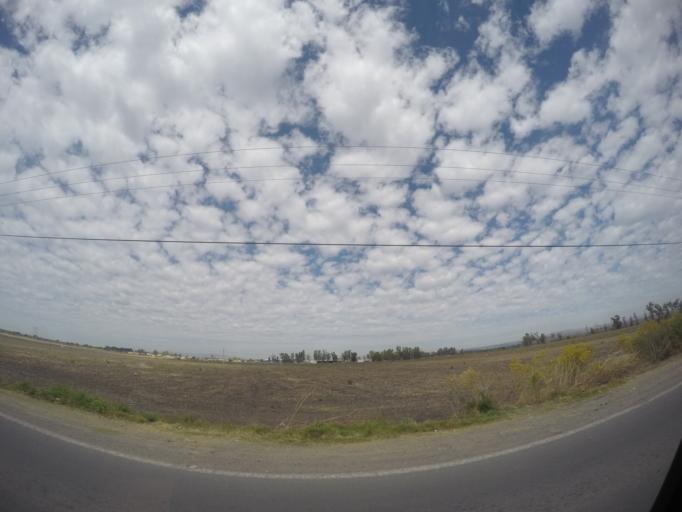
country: MX
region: Guanajuato
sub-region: Leon
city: Colonia Latinoamericana
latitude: 21.0318
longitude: -101.6950
